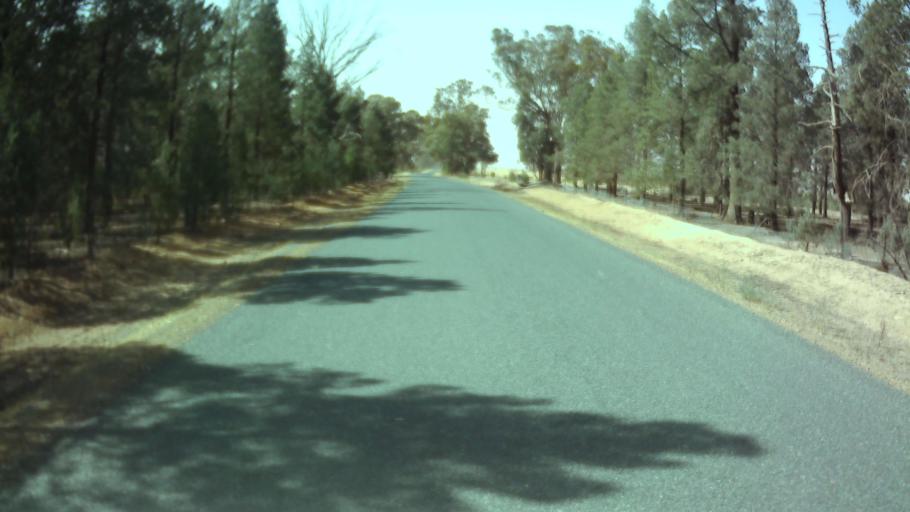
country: AU
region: New South Wales
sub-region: Weddin
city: Grenfell
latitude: -33.8998
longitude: 147.9210
